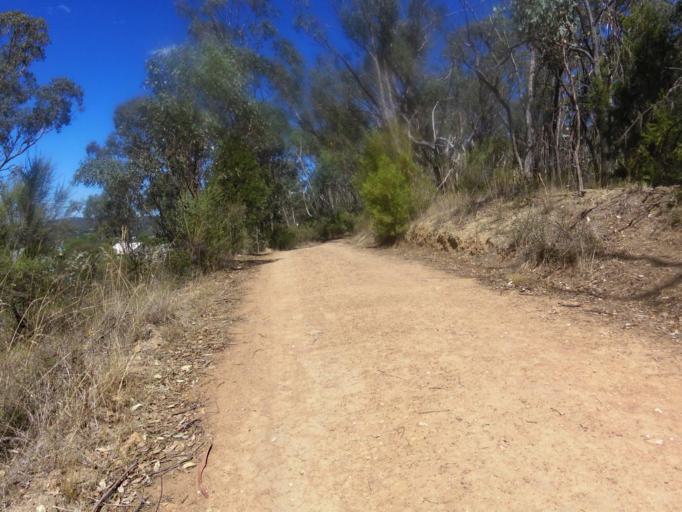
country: AU
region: Victoria
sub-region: Mount Alexander
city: Castlemaine
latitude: -37.0630
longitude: 144.1929
